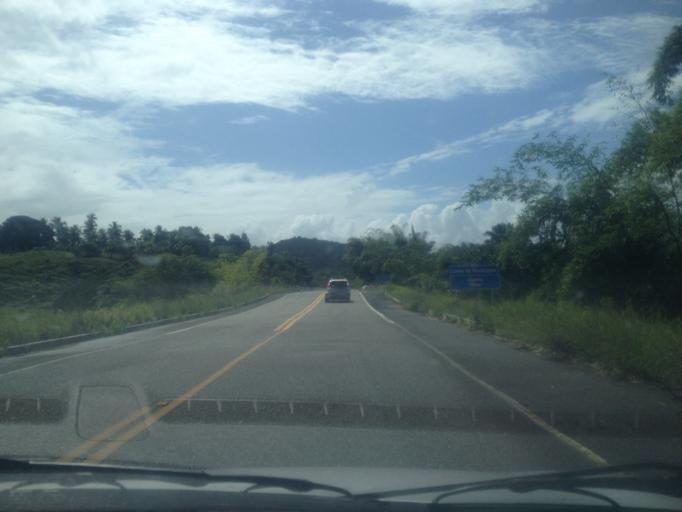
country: BR
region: Bahia
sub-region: Conde
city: Conde
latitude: -11.6950
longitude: -37.5709
